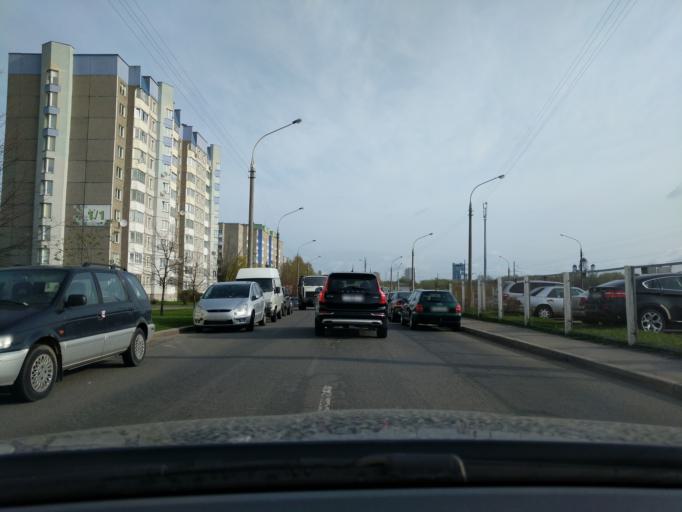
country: BY
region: Minsk
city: Novoye Medvezhino
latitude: 53.8979
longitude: 27.4632
